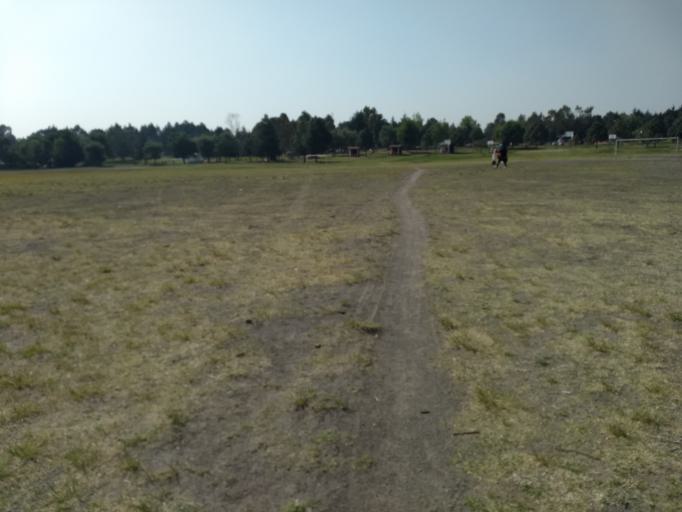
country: MX
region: Mexico
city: San Buenaventura
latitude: 19.2770
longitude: -99.6927
